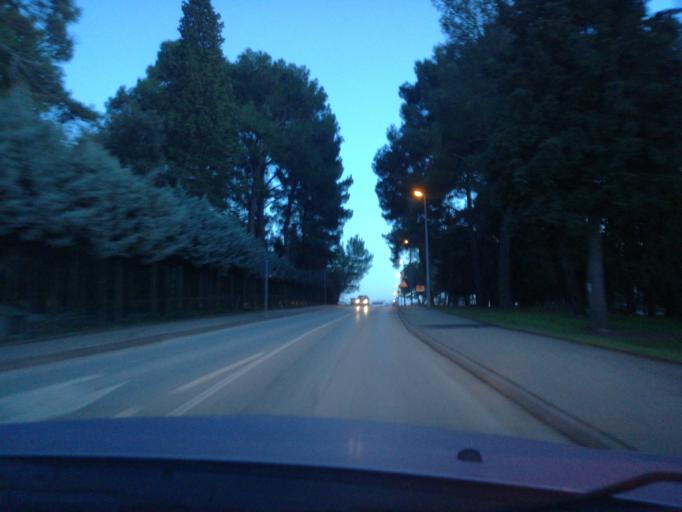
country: HR
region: Istarska
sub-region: Grad Rovinj
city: Rovinj
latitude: 45.0936
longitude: 13.6432
